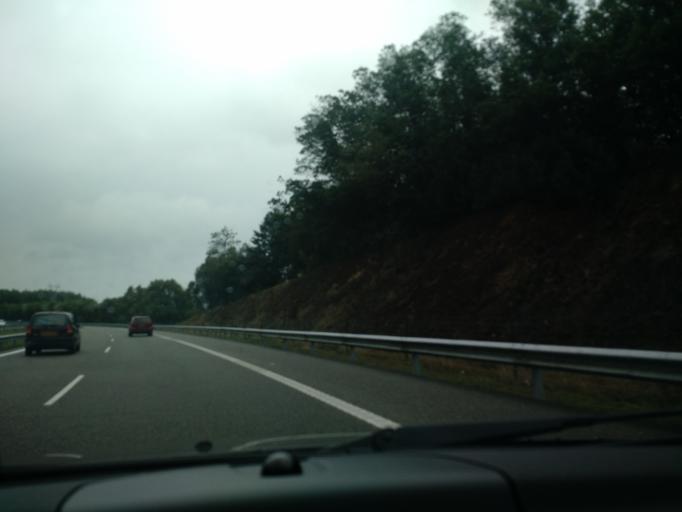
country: ES
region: Galicia
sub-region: Provincia da Coruna
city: Mesia
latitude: 43.1201
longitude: -8.3292
